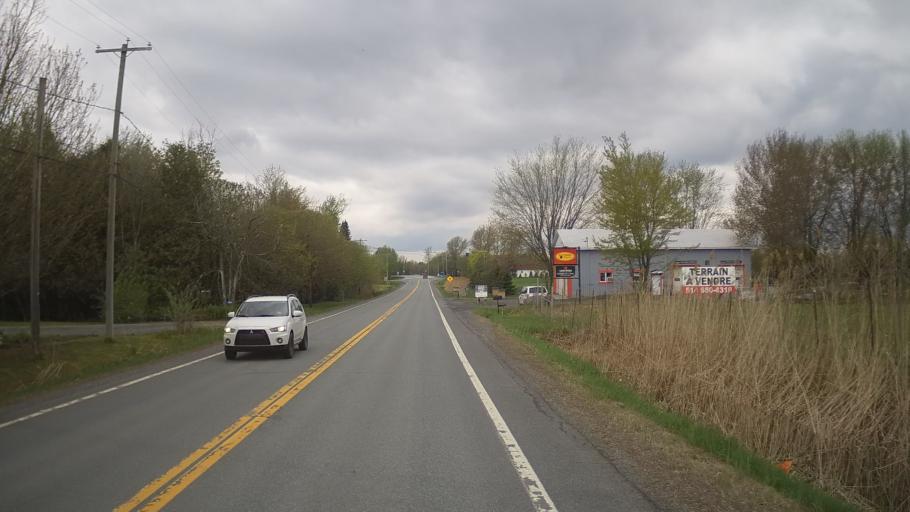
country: CA
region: Quebec
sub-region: Monteregie
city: Farnham
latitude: 45.2686
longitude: -72.9450
